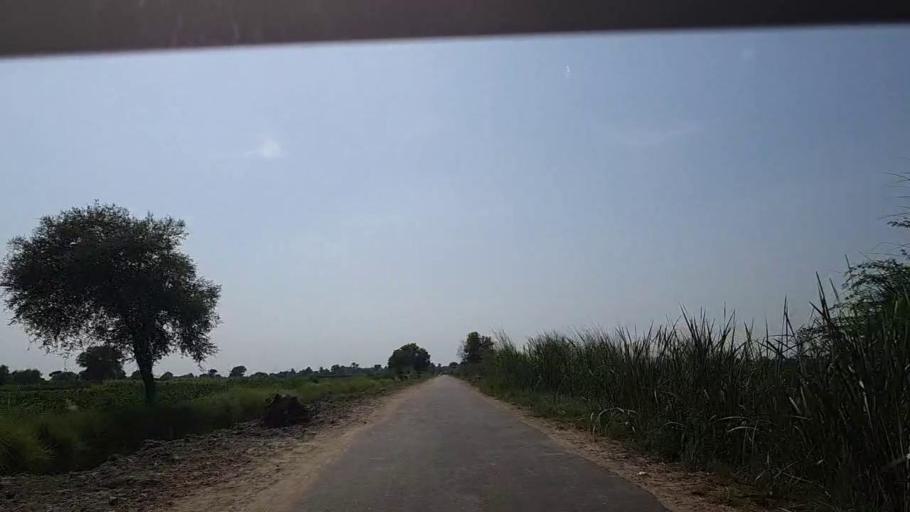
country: PK
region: Sindh
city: Khanpur
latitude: 27.8434
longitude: 69.4072
